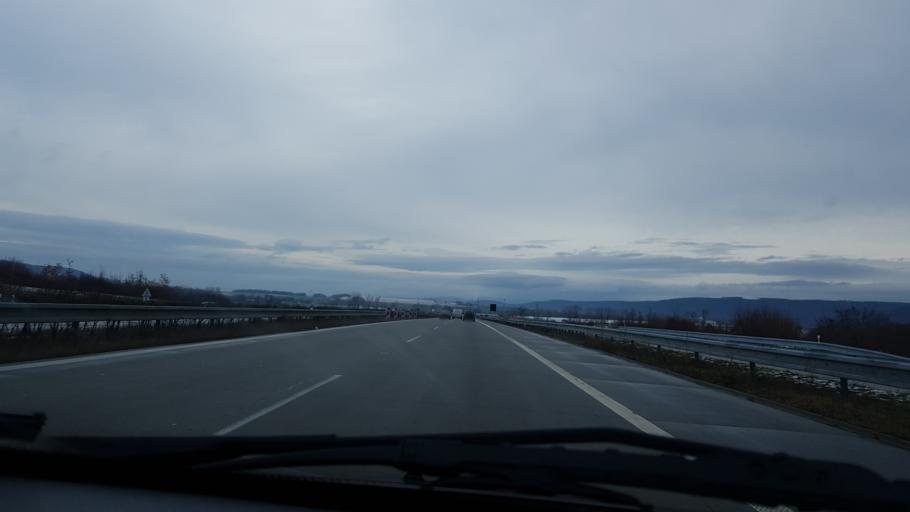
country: CZ
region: Olomoucky
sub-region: Okres Prerov
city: Lipnik nad Becvou
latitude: 49.5474
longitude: 17.5816
